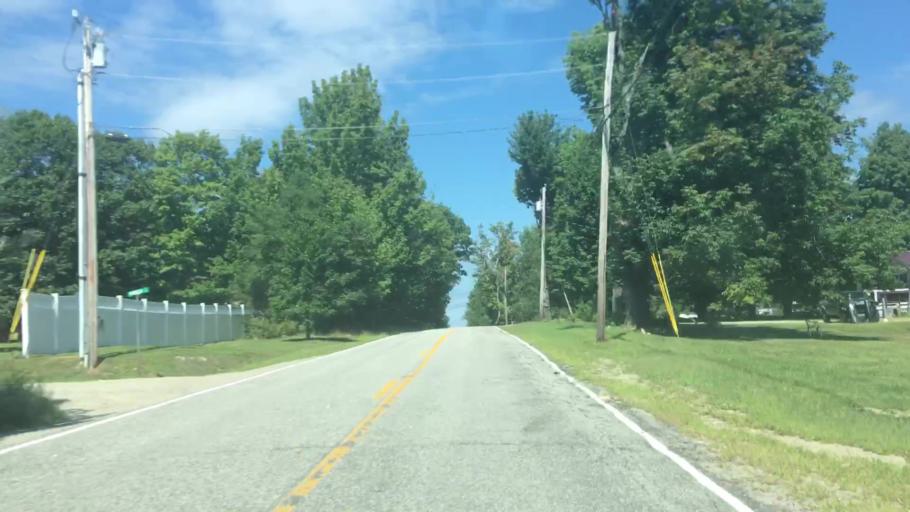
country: US
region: Maine
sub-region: Kennebec County
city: Monmouth
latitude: 44.1694
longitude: -69.9423
